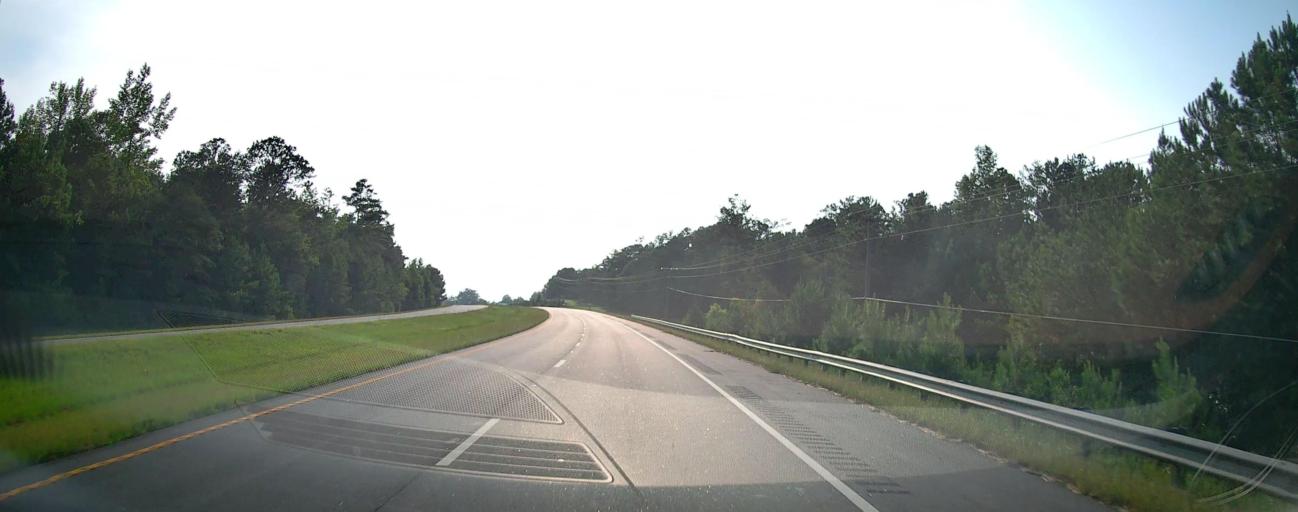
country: US
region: Georgia
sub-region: Talbot County
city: Talbotton
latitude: 32.5658
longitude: -84.6308
